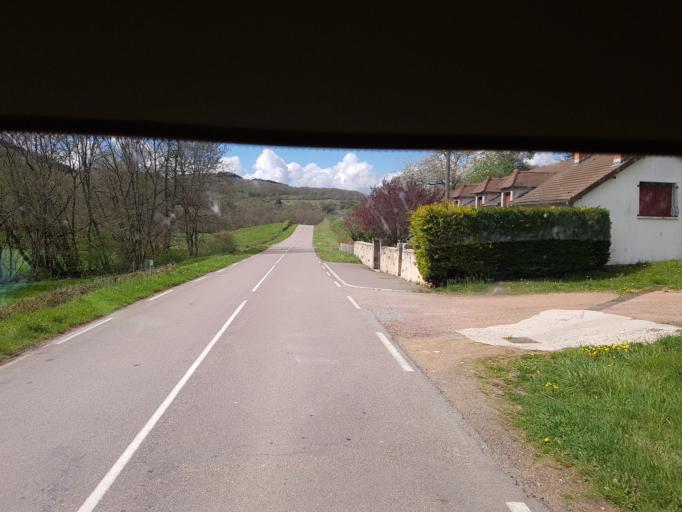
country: FR
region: Bourgogne
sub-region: Departement de Saone-et-Loire
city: Autun
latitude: 47.0954
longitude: 4.2348
